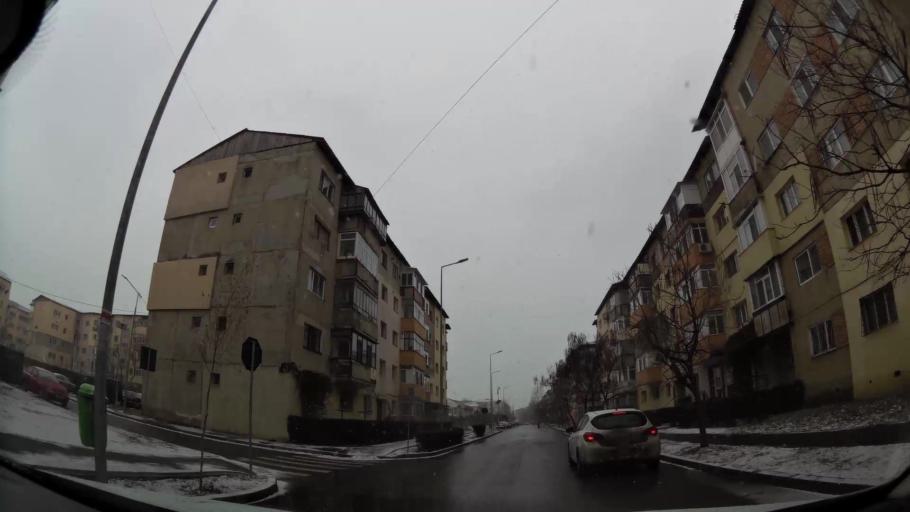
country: RO
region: Dambovita
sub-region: Municipiul Targoviste
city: Targoviste
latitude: 44.9176
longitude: 25.4793
